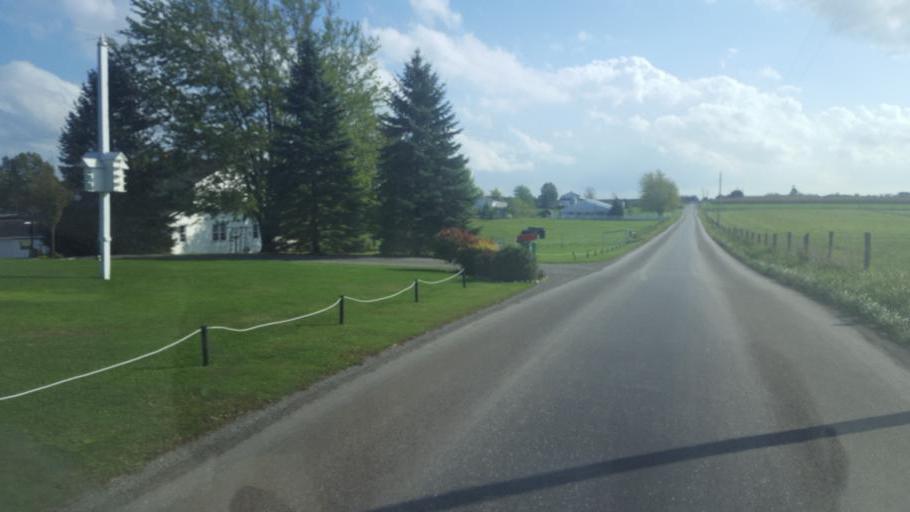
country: US
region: Ohio
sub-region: Wayne County
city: Apple Creek
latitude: 40.6559
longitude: -81.8419
